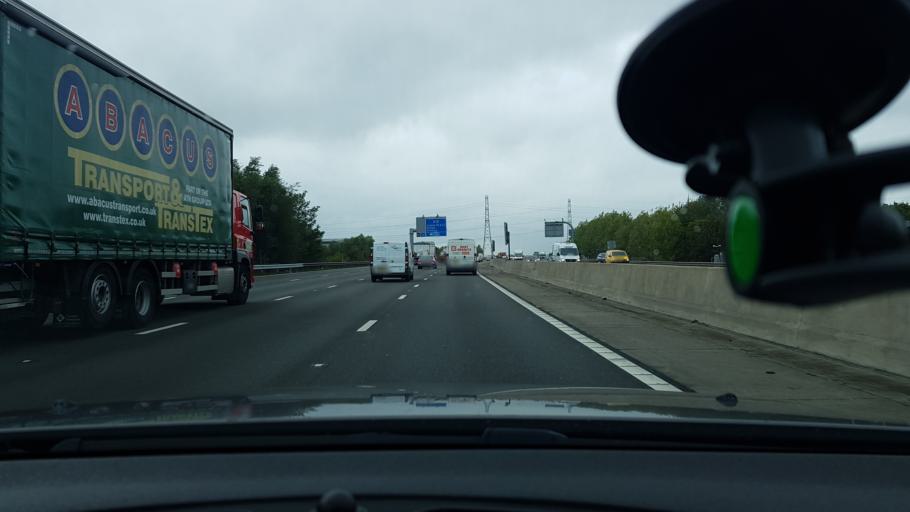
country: GB
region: England
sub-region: Essex
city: Waltham Abbey
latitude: 51.6807
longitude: -0.0035
